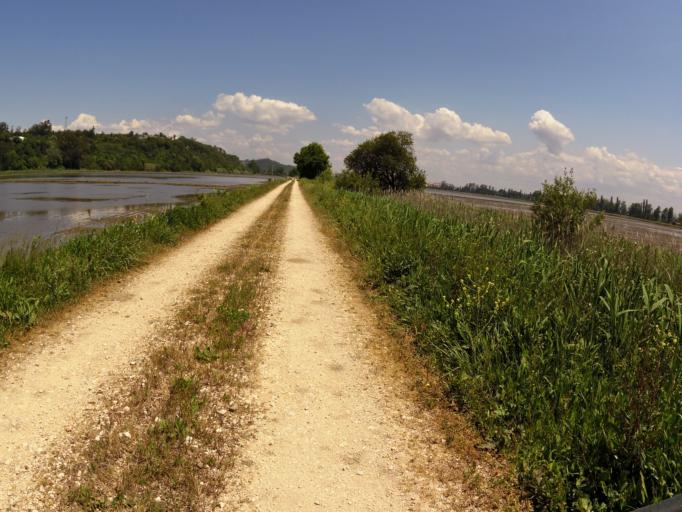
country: PT
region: Coimbra
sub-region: Montemor-O-Velho
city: Montemor-o-Velho
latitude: 40.1682
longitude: -8.7105
